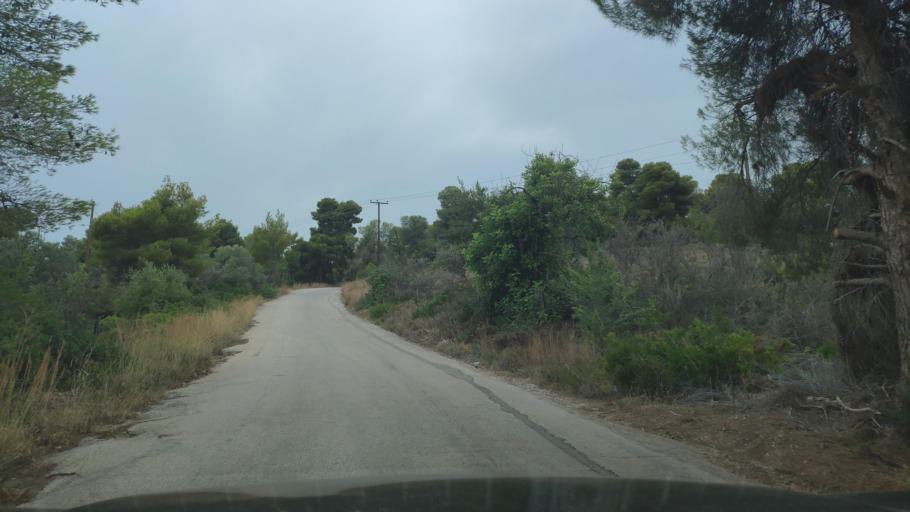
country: GR
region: Peloponnese
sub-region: Nomos Argolidos
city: Porto Cheli
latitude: 37.3078
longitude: 23.1532
